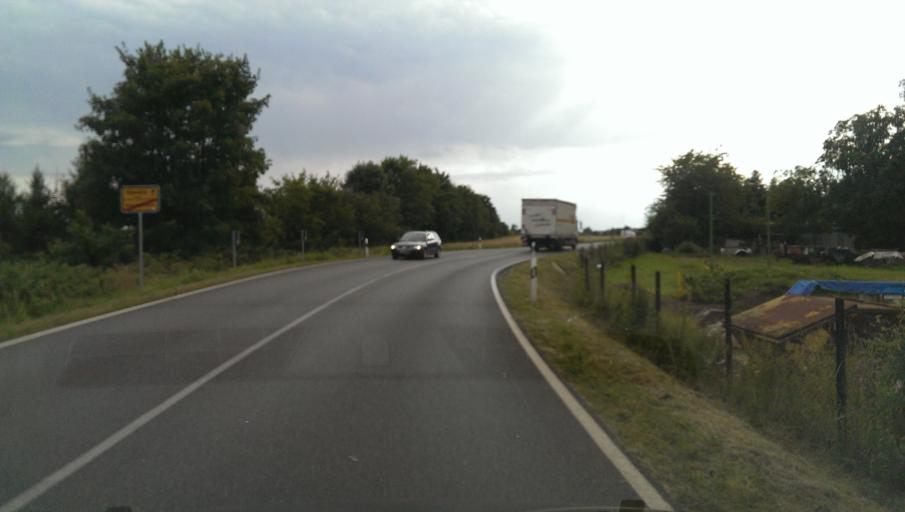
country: DE
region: Saxony
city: Groitzsch
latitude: 51.1839
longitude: 12.3044
